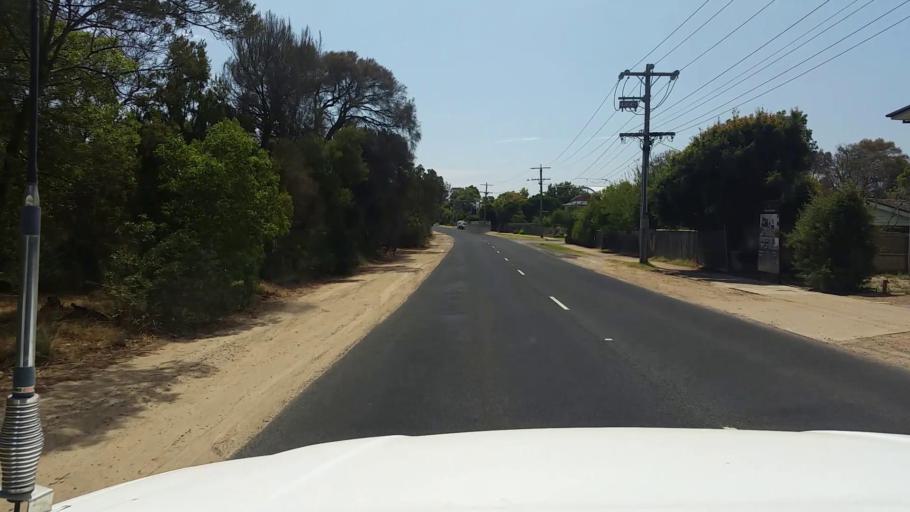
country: AU
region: Victoria
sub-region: Mornington Peninsula
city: Mount Martha
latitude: -38.2525
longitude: 145.0271
